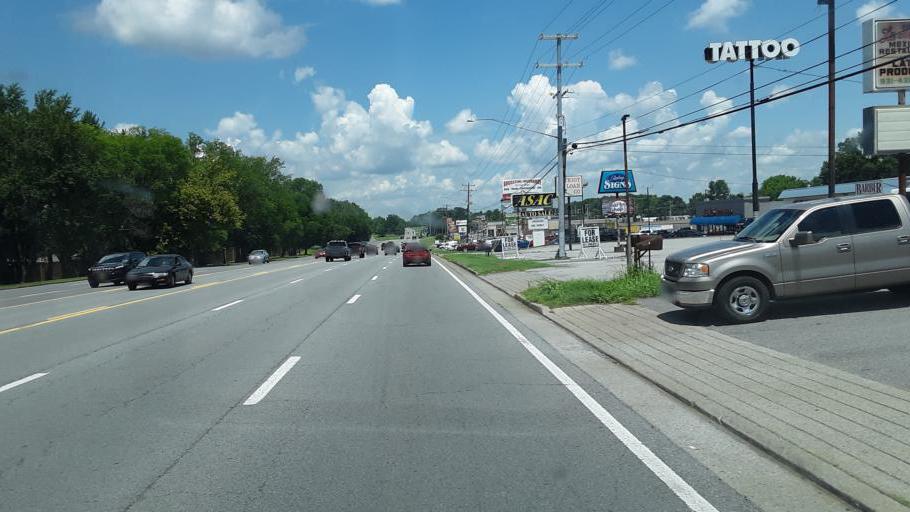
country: US
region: Kentucky
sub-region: Christian County
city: Fort Campbell North
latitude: 36.6250
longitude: -87.4327
